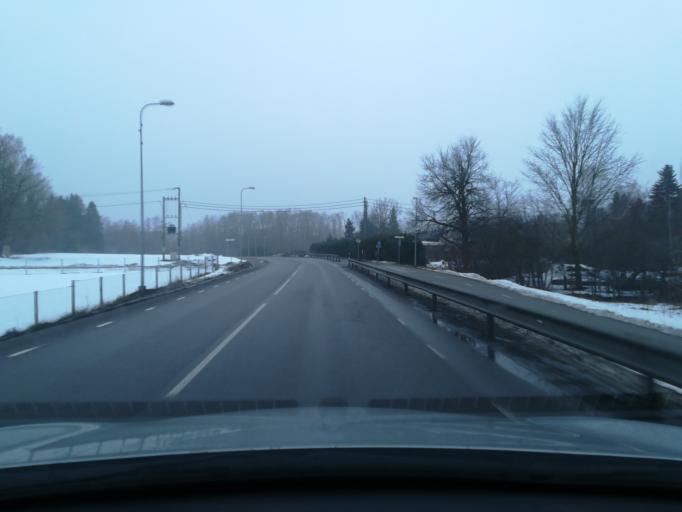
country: EE
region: Harju
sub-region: Rae vald
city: Jueri
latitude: 59.3623
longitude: 24.9467
